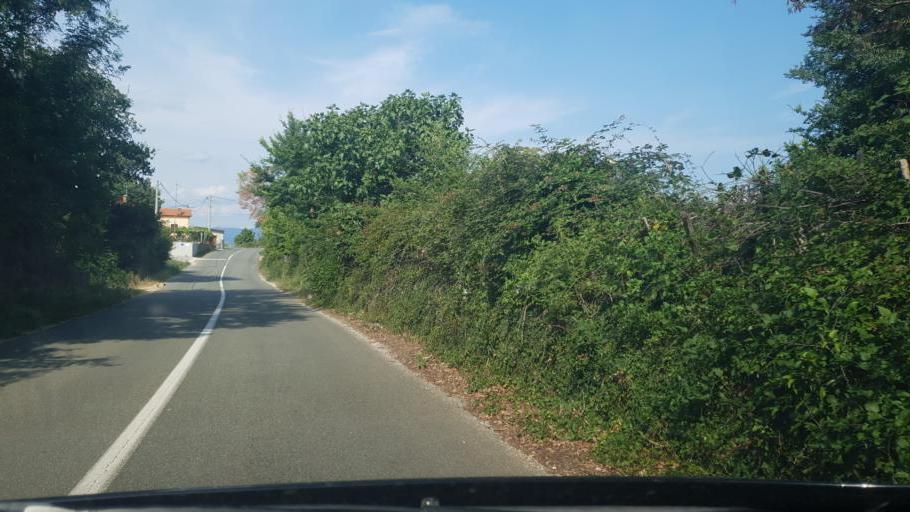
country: HR
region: Primorsko-Goranska
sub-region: Grad Crikvenica
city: Crikvenica
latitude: 45.1028
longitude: 14.6437
